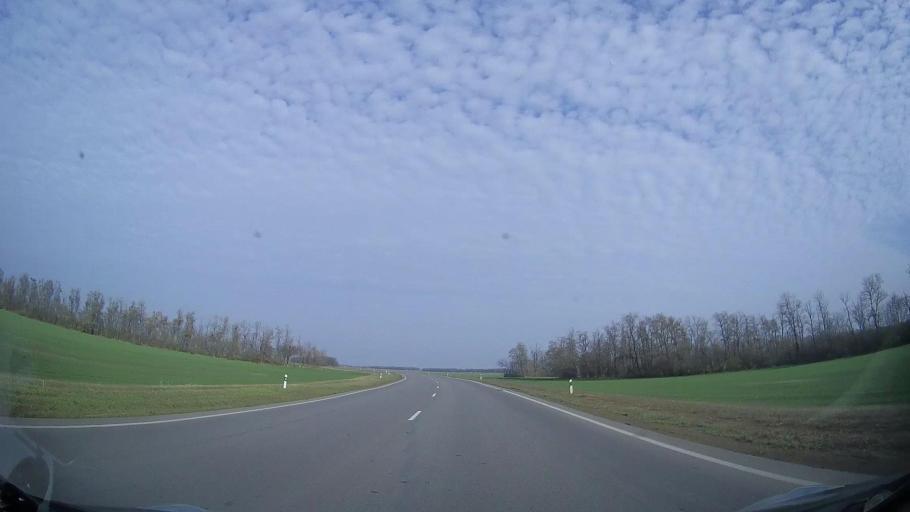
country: RU
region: Rostov
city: Tselina
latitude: 46.5156
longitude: 41.0712
